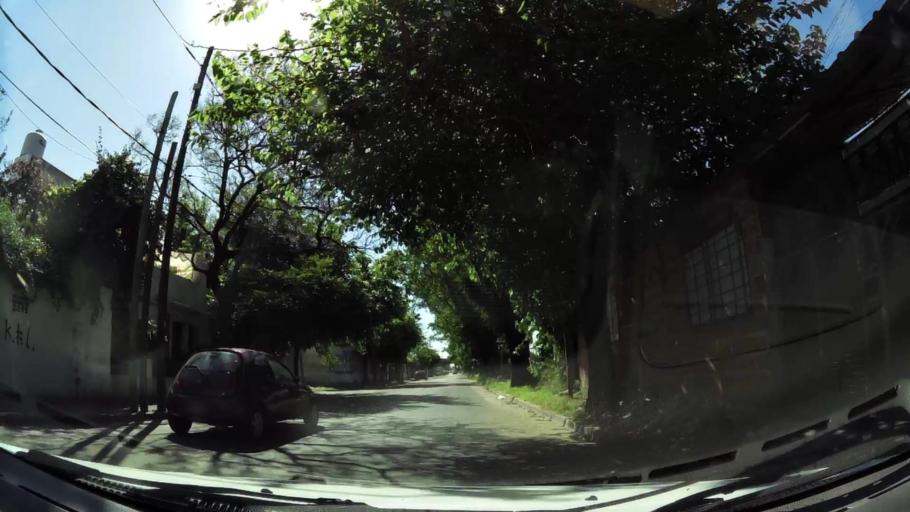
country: AR
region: Buenos Aires
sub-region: Partido de General San Martin
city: General San Martin
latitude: -34.5361
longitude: -58.5748
